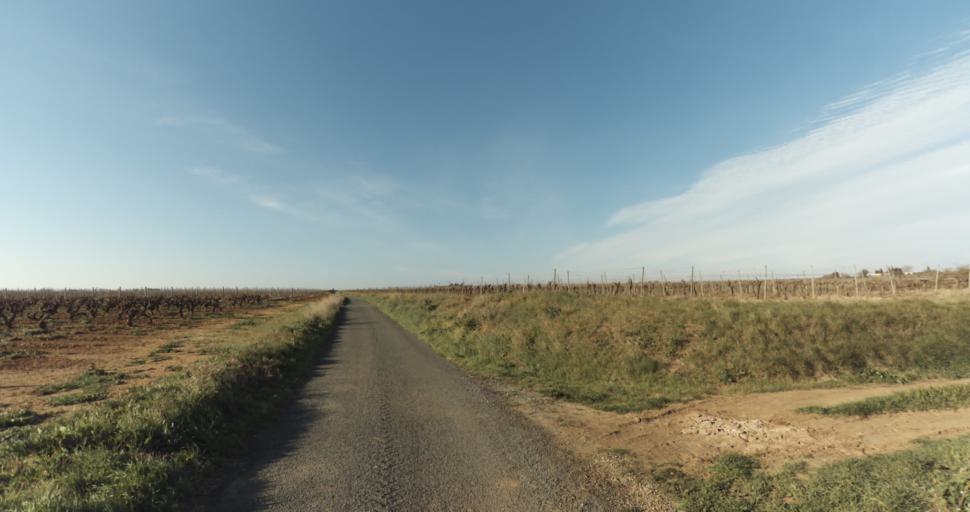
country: FR
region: Languedoc-Roussillon
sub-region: Departement de l'Herault
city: Marseillan
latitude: 43.3699
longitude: 3.5171
